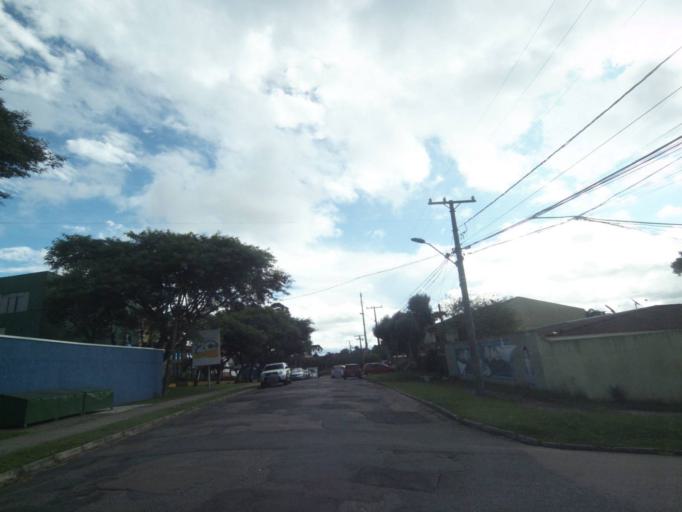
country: BR
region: Parana
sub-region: Curitiba
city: Curitiba
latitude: -25.4899
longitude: -49.2743
